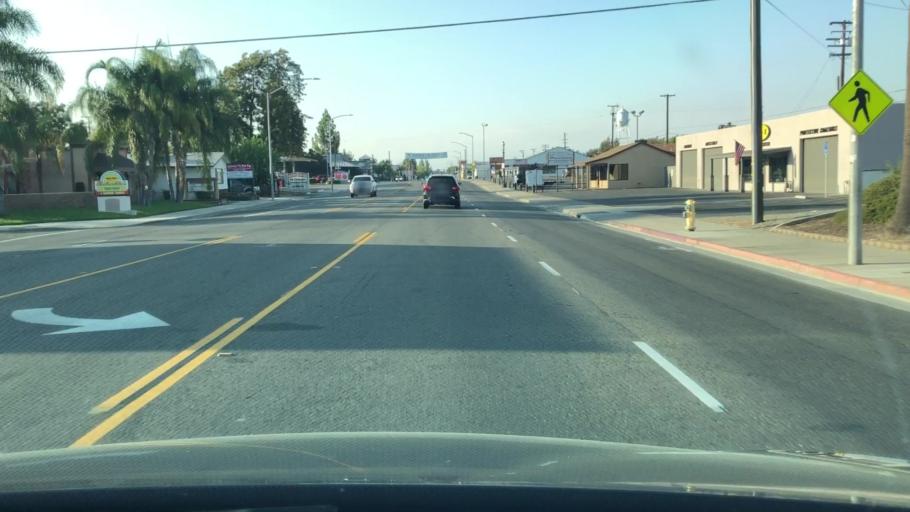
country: US
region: California
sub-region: Fresno County
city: Clovis
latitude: 36.8192
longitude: -119.7006
